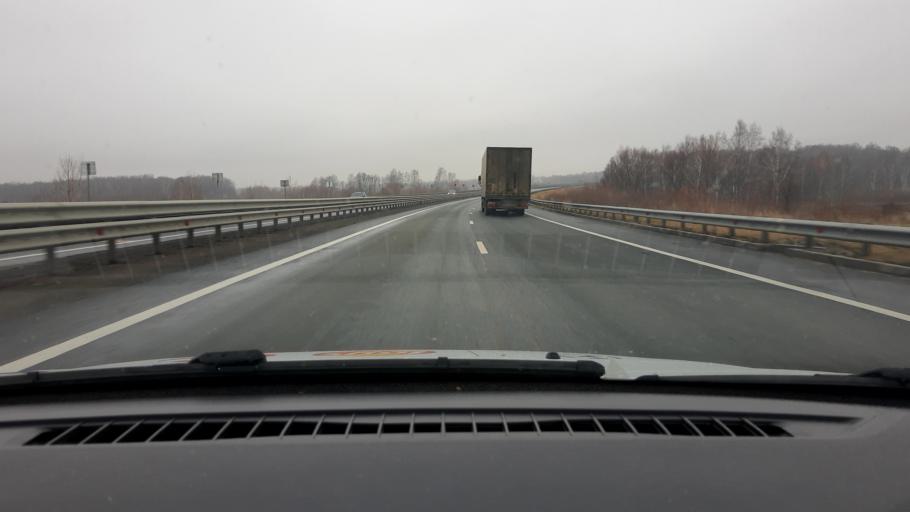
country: RU
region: Nizjnij Novgorod
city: Burevestnik
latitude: 56.1255
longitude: 43.7913
